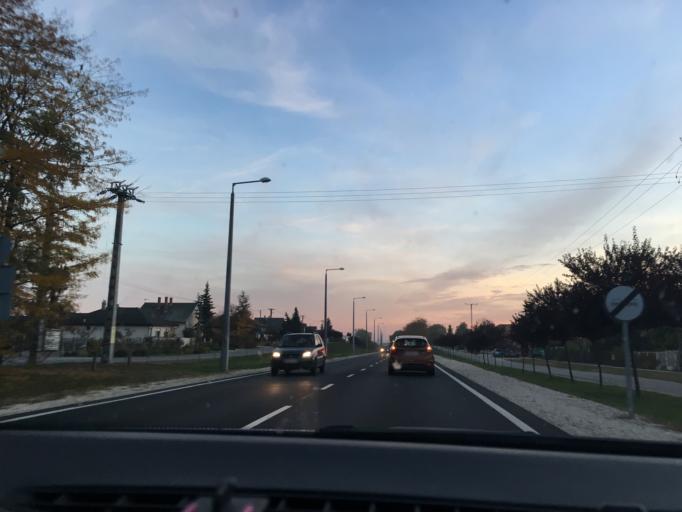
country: HU
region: Hajdu-Bihar
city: Hajduhadhaz
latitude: 47.6424
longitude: 21.6595
